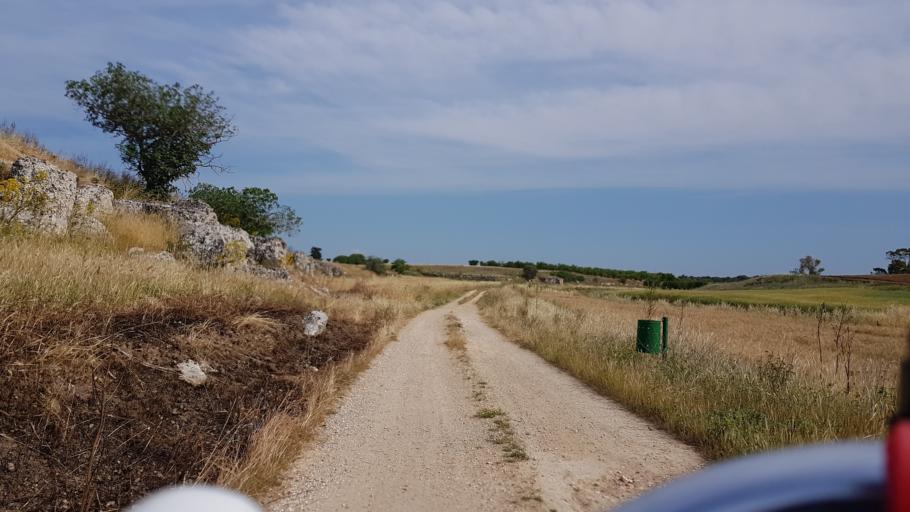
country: IT
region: Apulia
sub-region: Provincia di Brindisi
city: San Vito dei Normanni
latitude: 40.6638
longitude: 17.7977
